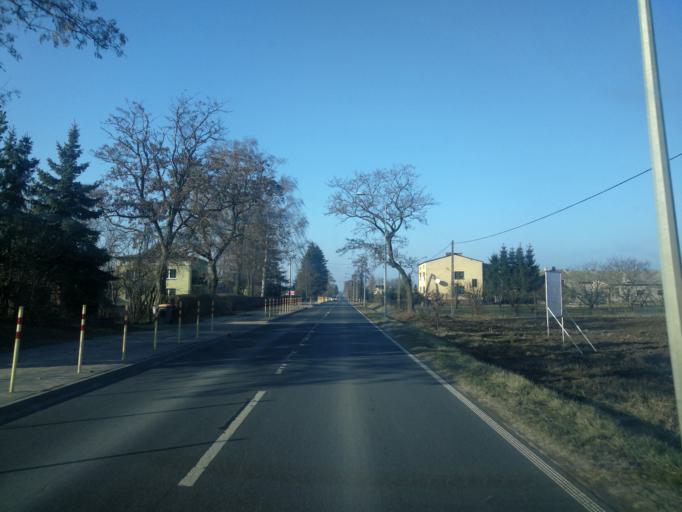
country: PL
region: Warmian-Masurian Voivodeship
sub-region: Powiat ilawski
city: Lubawa
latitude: 53.4753
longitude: 19.7665
